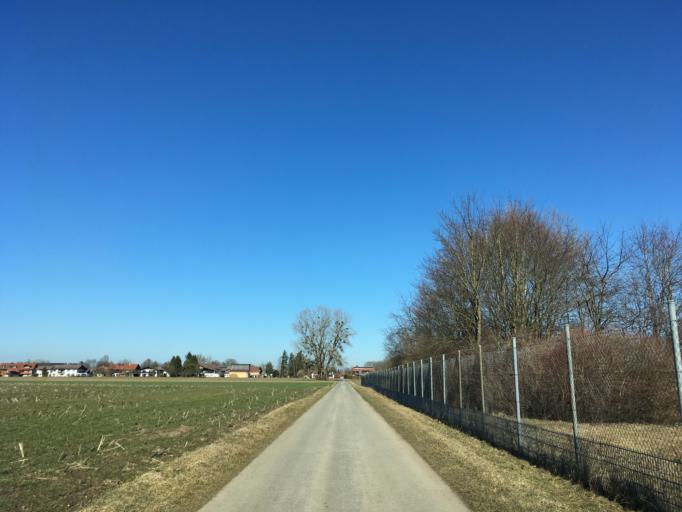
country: DE
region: Bavaria
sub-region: Upper Bavaria
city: Bad Aibling
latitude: 47.8495
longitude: 11.9892
